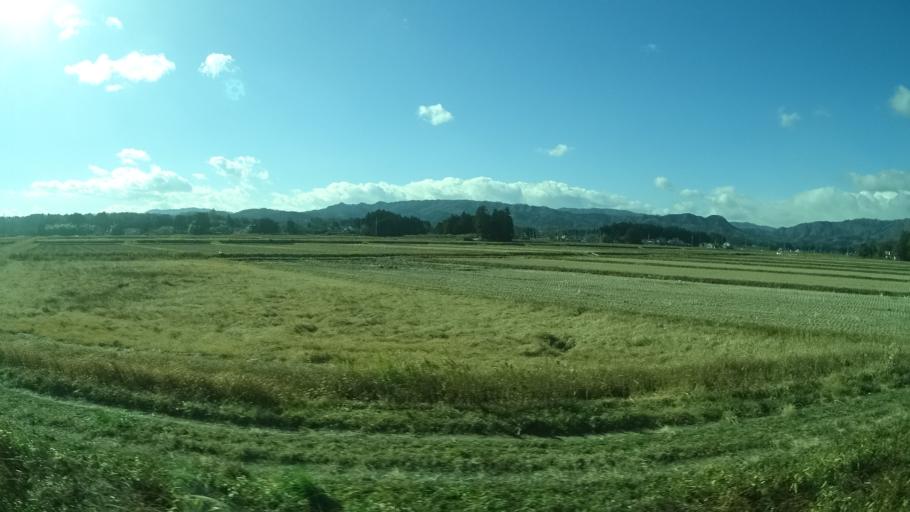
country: JP
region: Miyagi
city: Marumori
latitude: 37.7717
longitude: 140.9207
